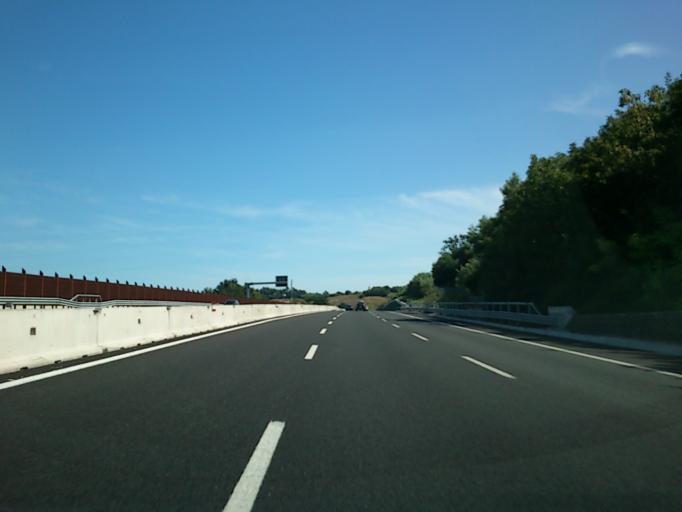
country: IT
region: The Marches
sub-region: Provincia di Pesaro e Urbino
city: Pesaro
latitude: 43.8878
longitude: 12.8953
